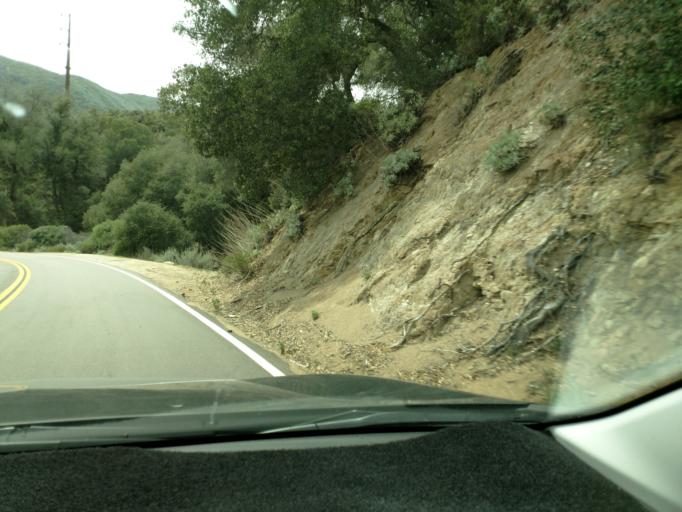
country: US
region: California
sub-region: Riverside County
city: Aguanga
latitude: 33.2418
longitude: -116.7644
